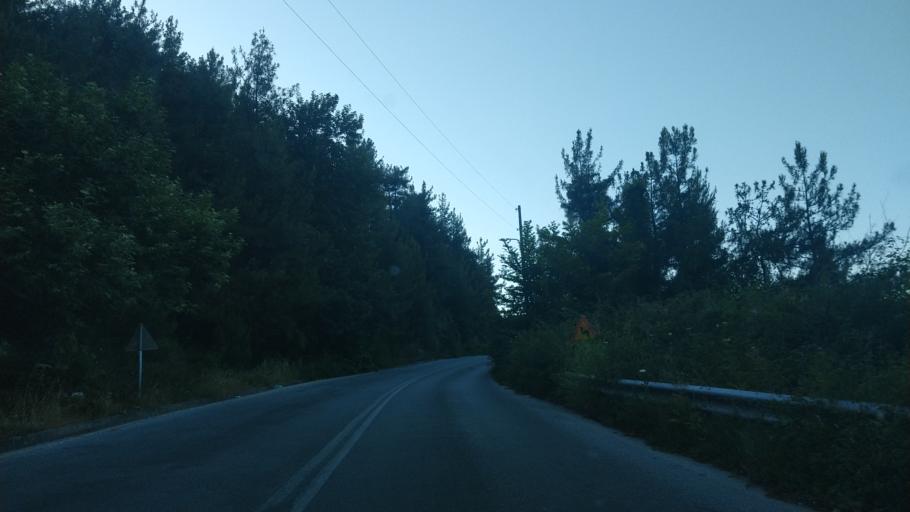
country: GR
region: East Macedonia and Thrace
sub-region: Nomos Kavalas
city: Potamia
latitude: 40.7280
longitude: 24.7326
